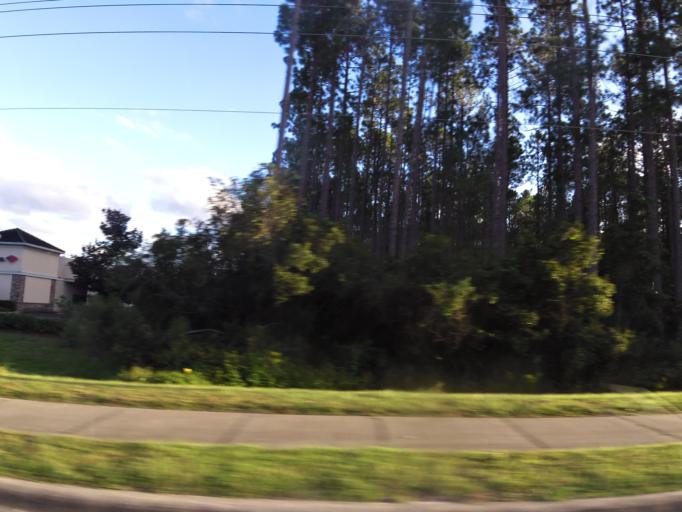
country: US
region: Florida
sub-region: Saint Johns County
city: Fruit Cove
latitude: 30.0591
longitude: -81.5333
